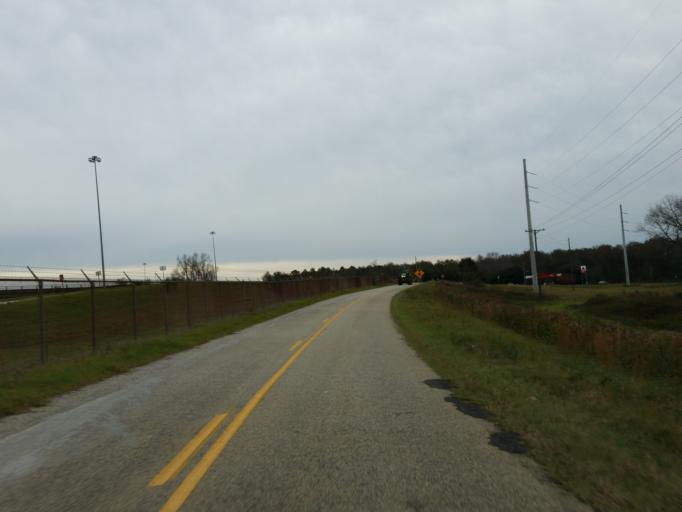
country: US
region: Georgia
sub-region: Dooly County
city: Vienna
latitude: 32.1245
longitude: -83.7615
